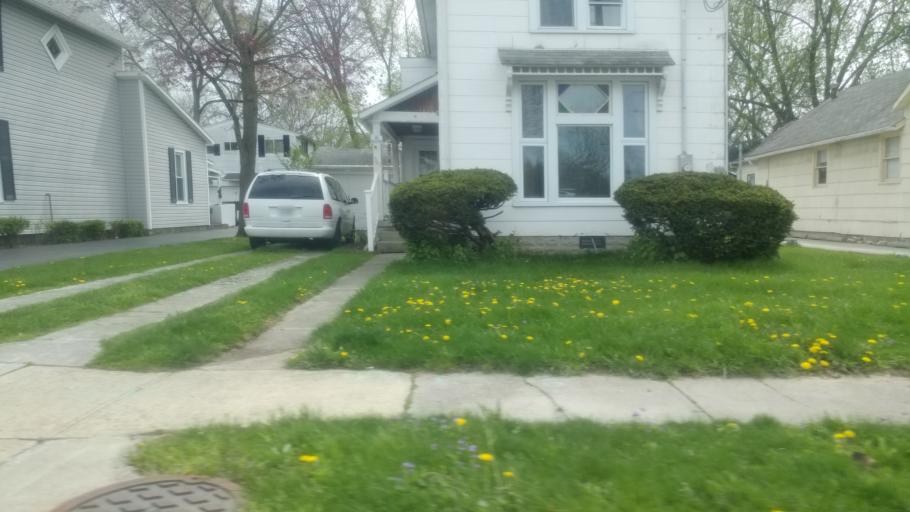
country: US
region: Ohio
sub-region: Wood County
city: Bowling Green
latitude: 41.3787
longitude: -83.6553
